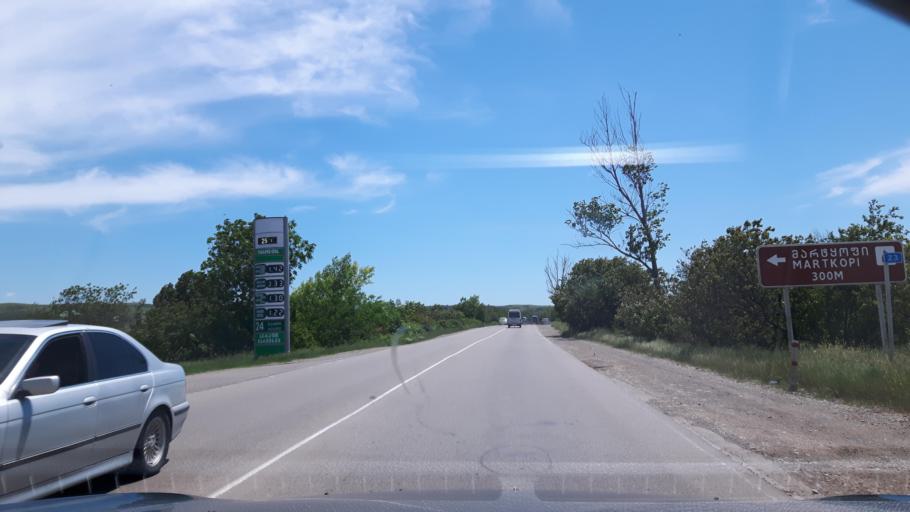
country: GE
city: Didi Lilo
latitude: 41.6981
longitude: 45.0478
